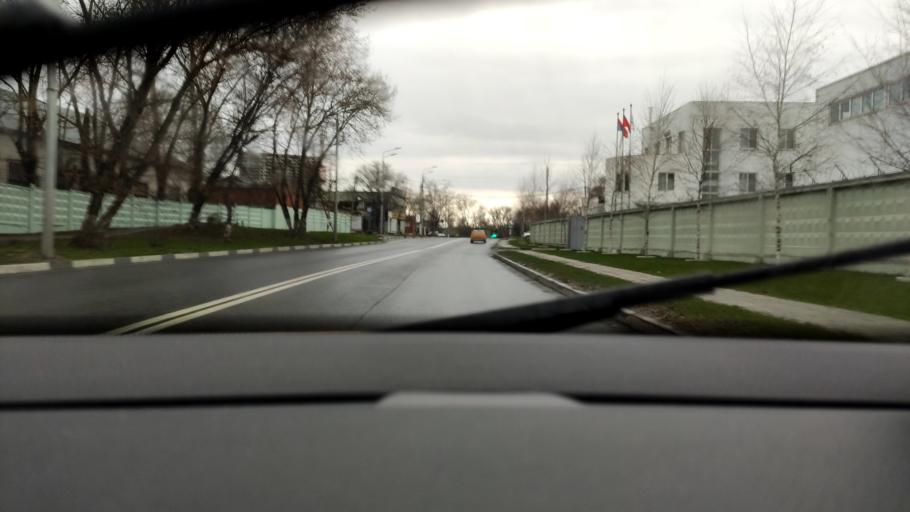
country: RU
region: Moskovskaya
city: Balashikha
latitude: 55.8327
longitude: 37.9469
